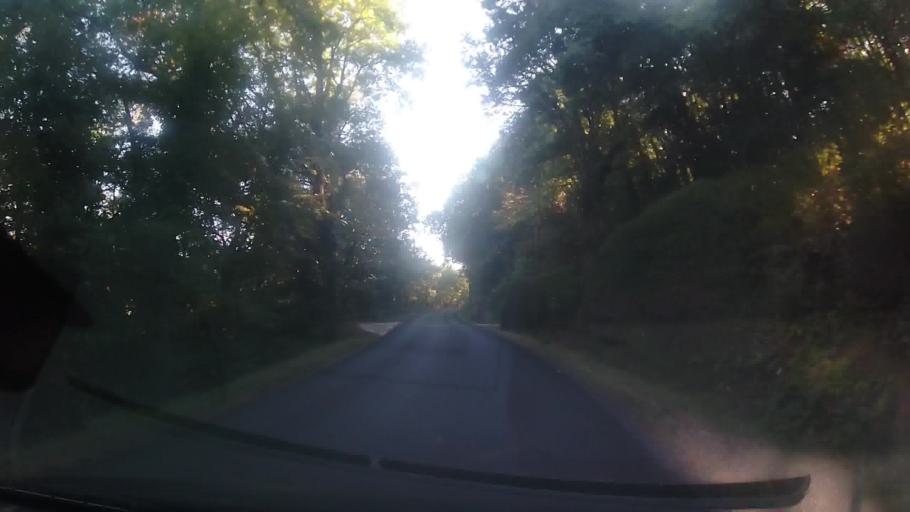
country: FR
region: Aquitaine
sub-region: Departement de la Dordogne
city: Cenac-et-Saint-Julien
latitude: 44.7921
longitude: 1.1879
